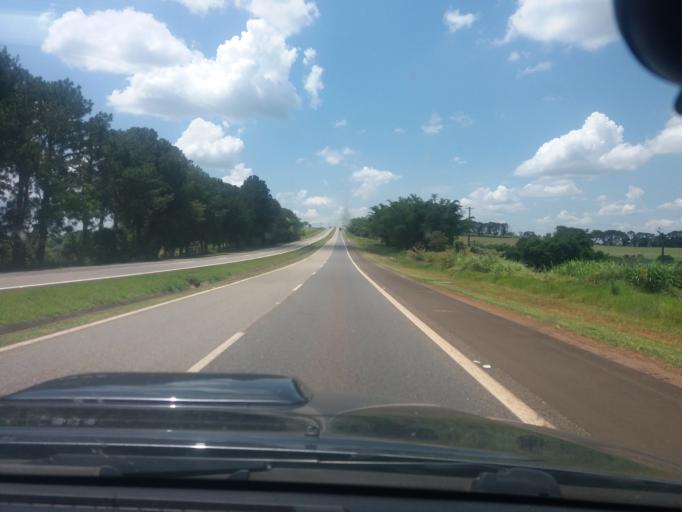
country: BR
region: Sao Paulo
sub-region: Itapetininga
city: Itapetininga
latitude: -23.5231
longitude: -47.9659
